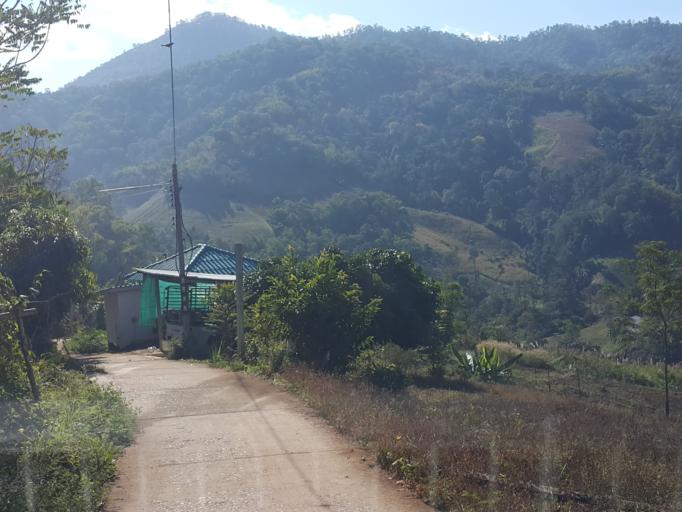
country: TH
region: Chiang Mai
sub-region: Amphoe Chiang Dao
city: Chiang Dao
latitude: 19.5221
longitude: 98.8626
